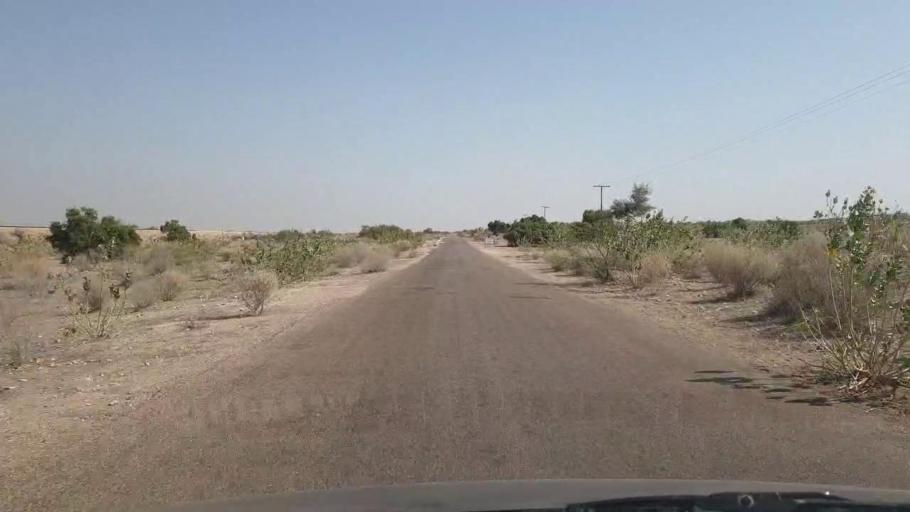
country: PK
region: Sindh
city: Chor
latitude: 25.5456
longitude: 69.8673
